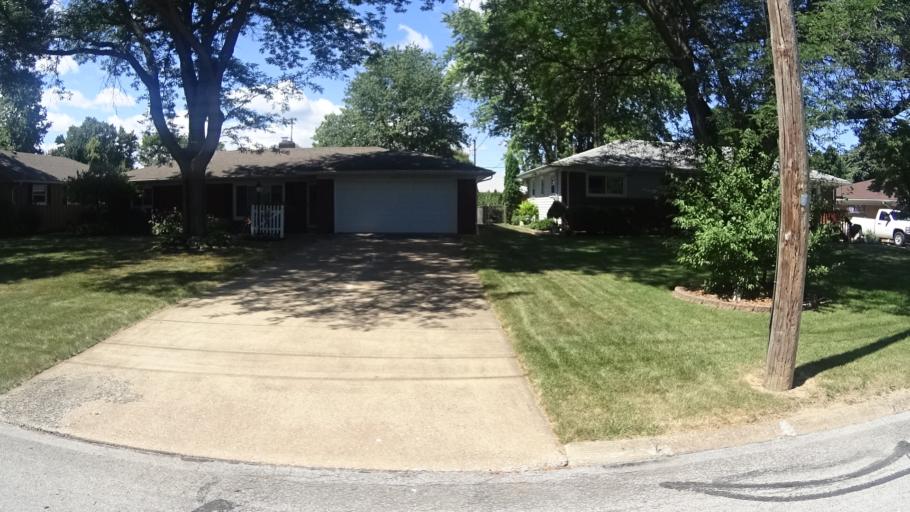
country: US
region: Ohio
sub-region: Erie County
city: Sandusky
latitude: 41.4294
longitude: -82.6834
